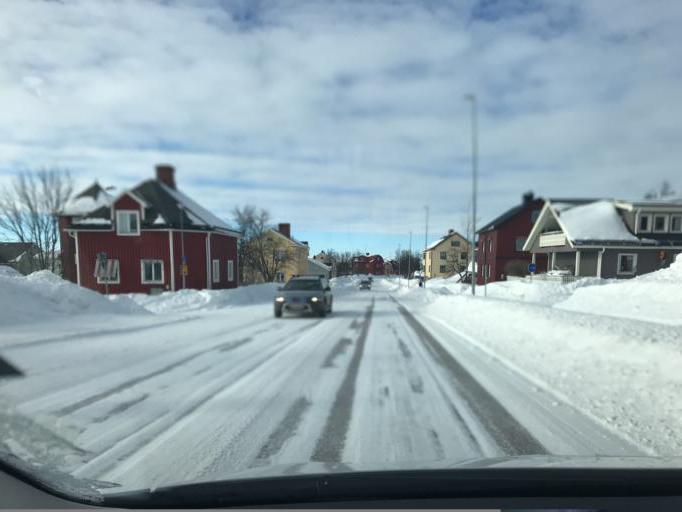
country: SE
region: Norrbotten
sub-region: Kiruna Kommun
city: Kiruna
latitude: 67.8600
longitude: 20.2213
